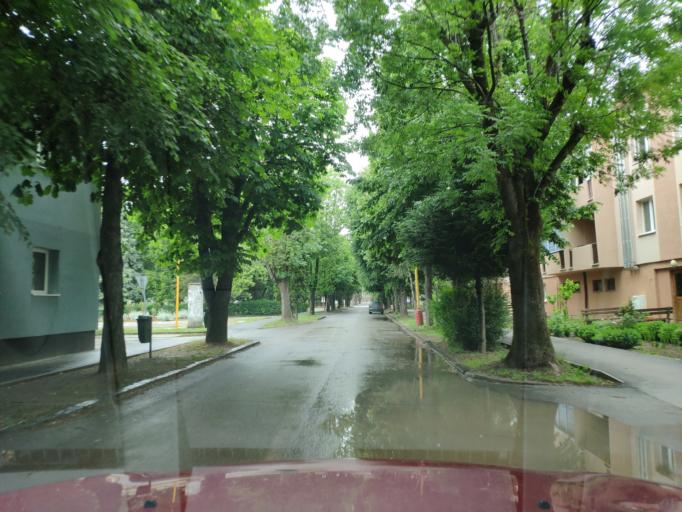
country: SK
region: Kosicky
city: Cierna nad Tisou
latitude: 48.4163
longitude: 22.0893
